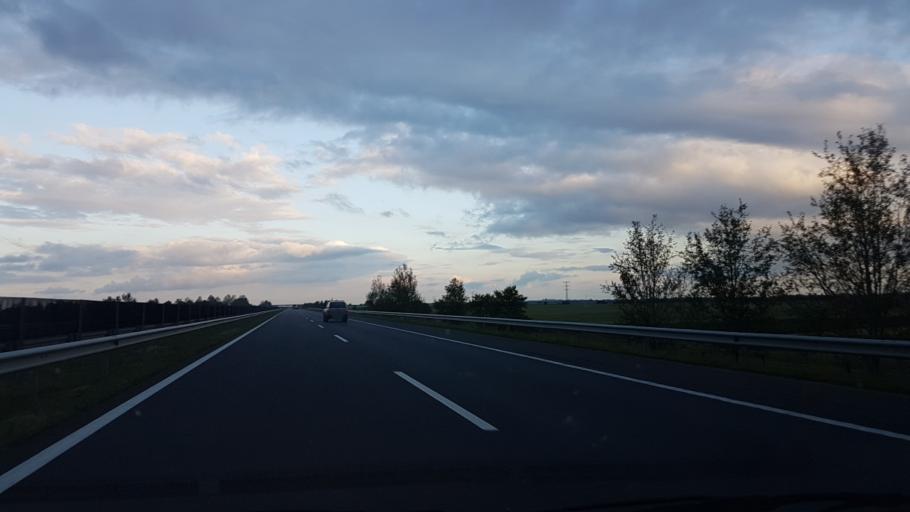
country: HU
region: Borsod-Abauj-Zemplen
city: Malyi
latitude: 48.0255
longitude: 20.8661
